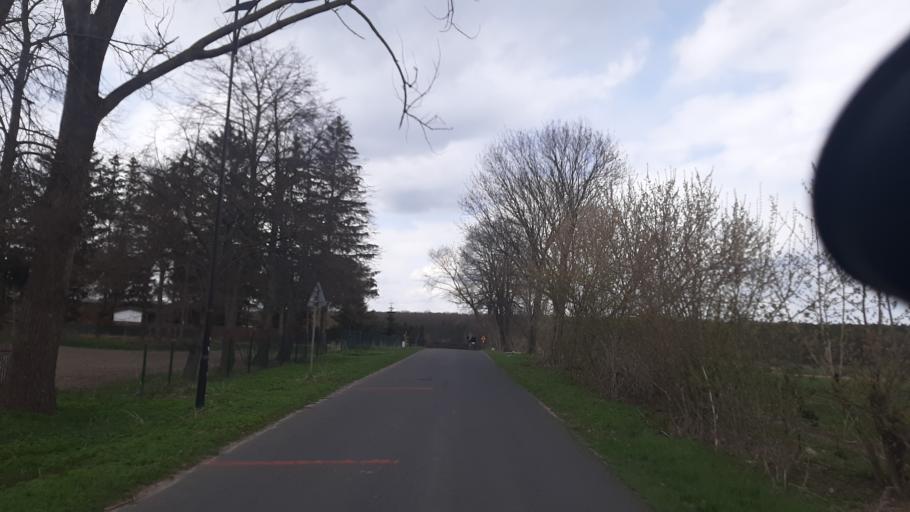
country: PL
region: Lublin Voivodeship
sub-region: Powiat lubelski
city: Niemce
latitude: 51.3640
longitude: 22.5539
